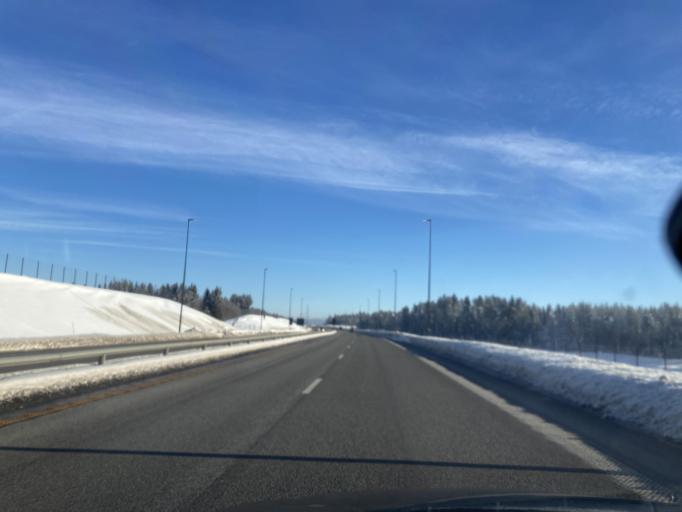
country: NO
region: Hedmark
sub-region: Loten
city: Loten
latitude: 60.8526
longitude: 11.3879
